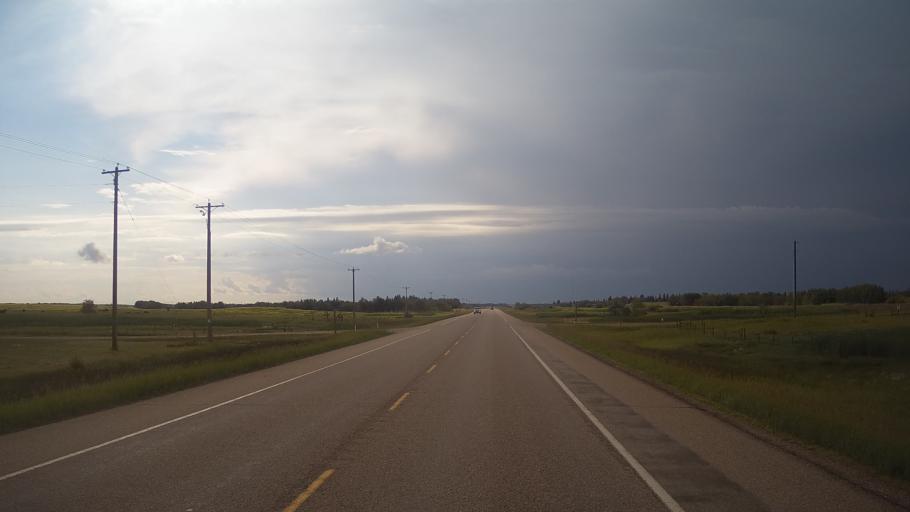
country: CA
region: Alberta
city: Viking
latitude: 53.1663
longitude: -112.0254
